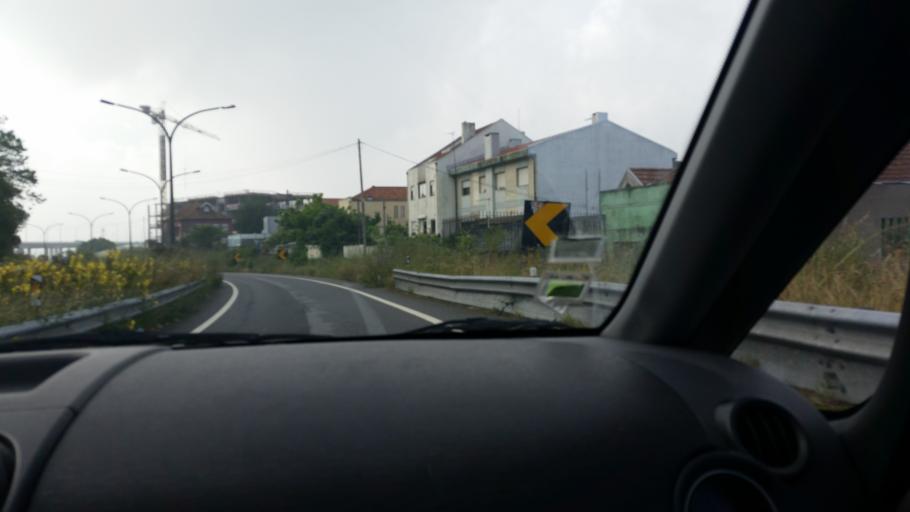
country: PT
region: Porto
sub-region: Vila Nova de Gaia
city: Canidelo
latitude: 41.1503
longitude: -8.6444
